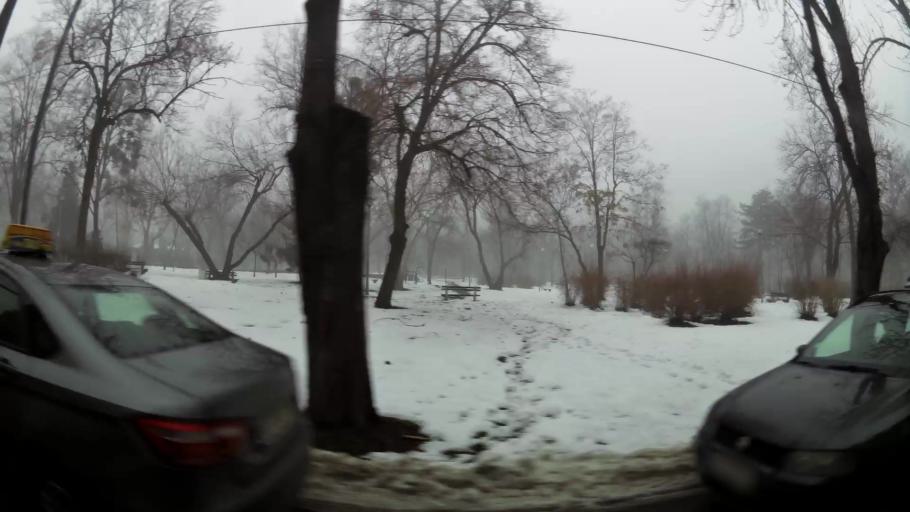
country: RS
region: Central Serbia
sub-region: Belgrade
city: Savski Venac
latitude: 44.7875
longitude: 20.4413
